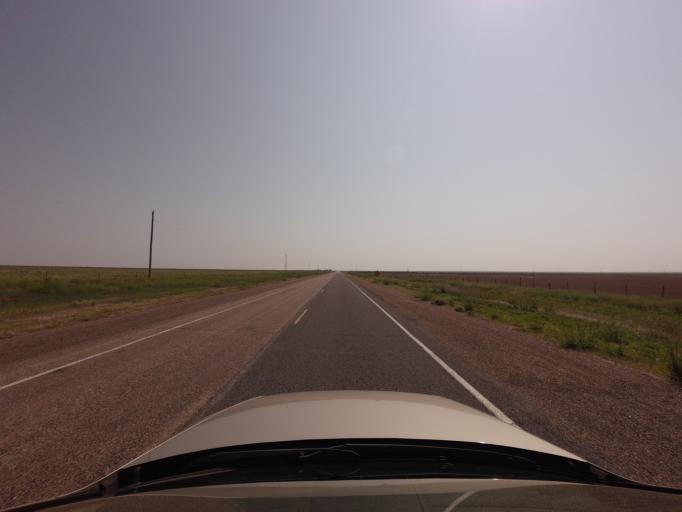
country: US
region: New Mexico
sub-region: Quay County
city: Tucumcari
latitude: 34.8234
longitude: -103.7283
